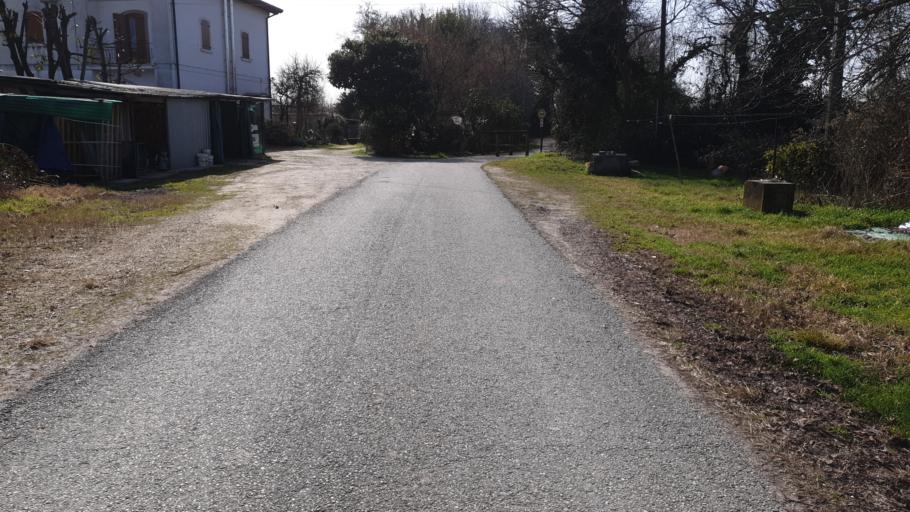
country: IT
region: Veneto
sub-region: Provincia di Padova
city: Camposampiero
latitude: 45.5633
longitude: 11.9256
